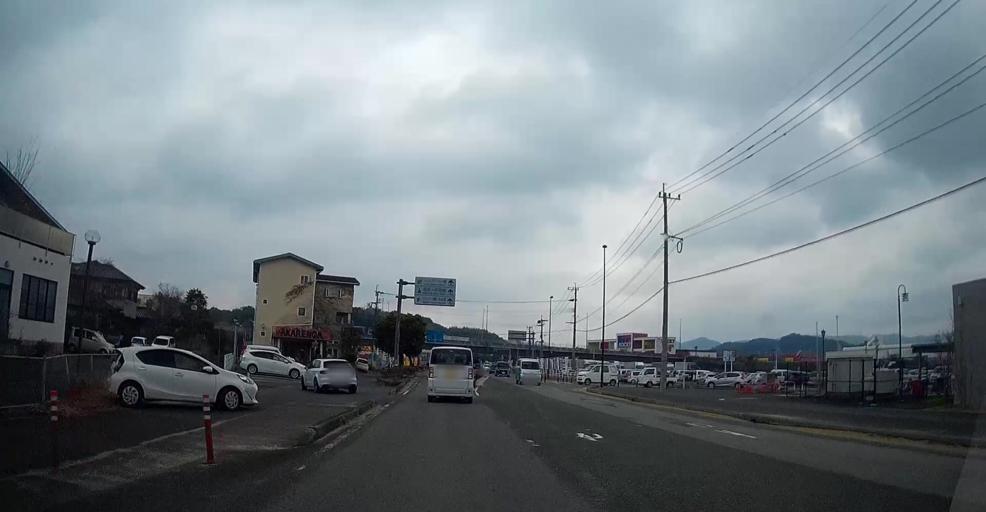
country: JP
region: Kumamoto
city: Matsubase
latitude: 32.6517
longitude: 130.6978
